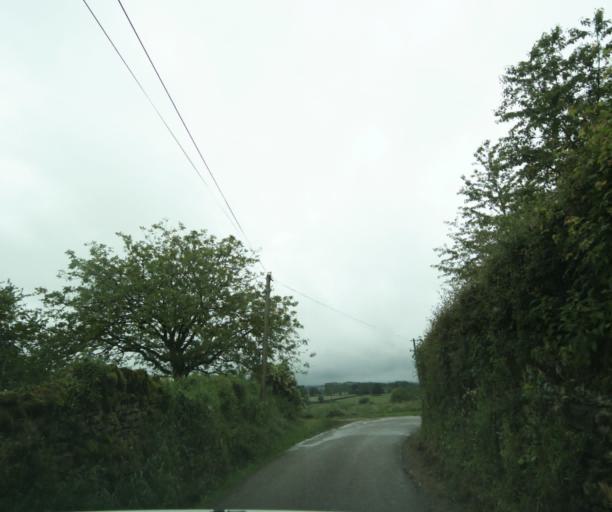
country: FR
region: Bourgogne
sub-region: Departement de Saone-et-Loire
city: Charolles
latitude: 46.3798
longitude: 4.2312
